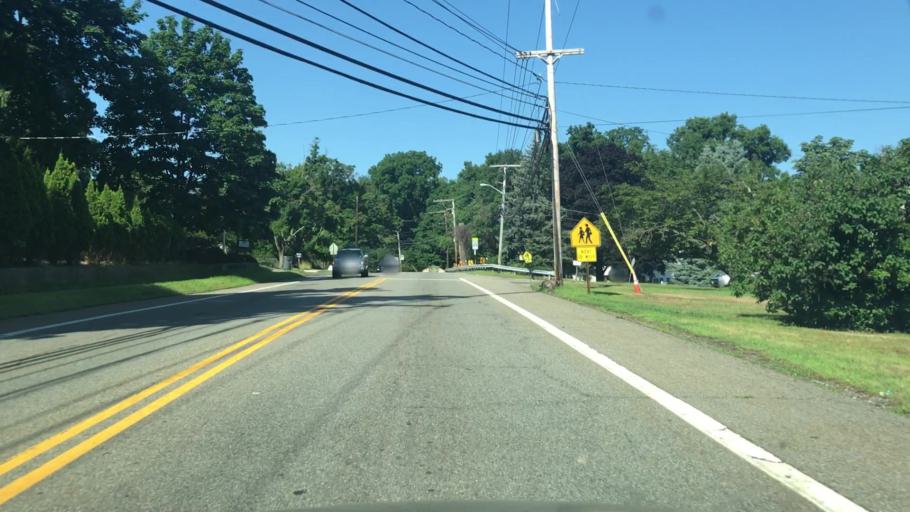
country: US
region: New Jersey
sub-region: Morris County
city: Parsippany
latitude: 40.8616
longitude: -74.4474
